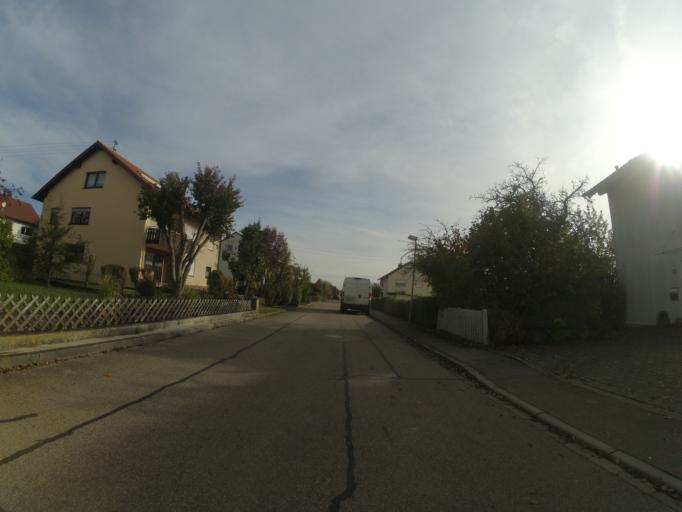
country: DE
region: Baden-Wuerttemberg
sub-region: Tuebingen Region
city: Blaubeuren
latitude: 48.4280
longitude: 9.8602
